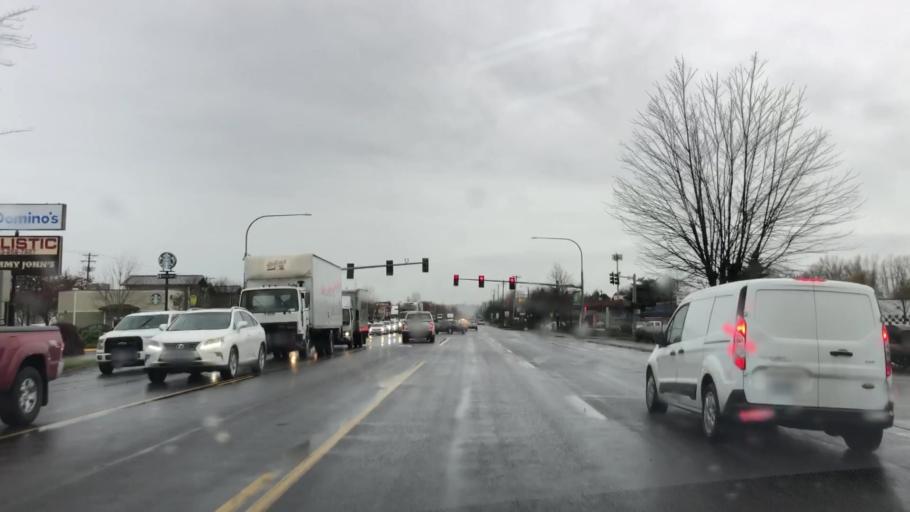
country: US
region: Washington
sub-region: Pierce County
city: Fife
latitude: 47.2431
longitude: -122.3638
